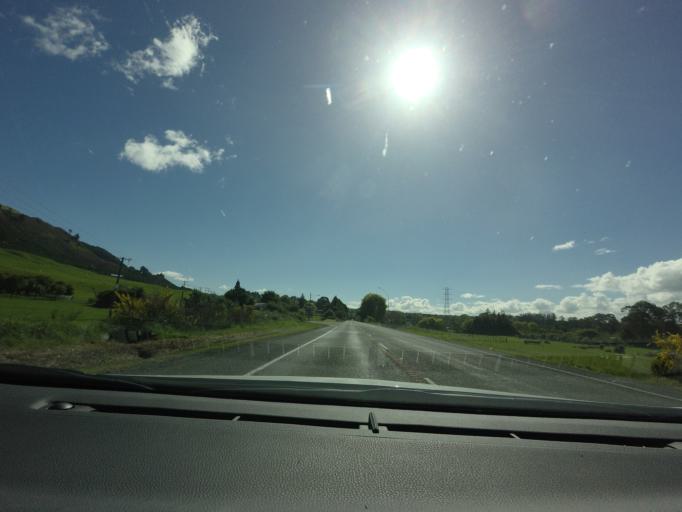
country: NZ
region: Bay of Plenty
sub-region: Rotorua District
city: Rotorua
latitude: -38.0882
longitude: 176.2023
